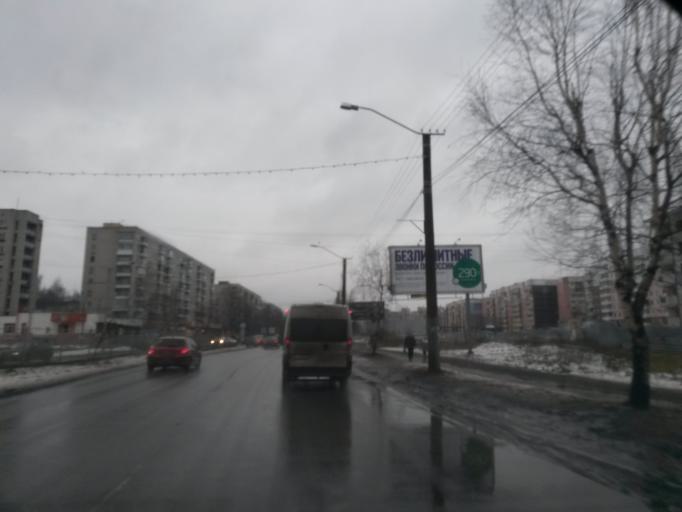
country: RU
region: Jaroslavl
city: Yaroslavl
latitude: 57.6459
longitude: 39.9544
